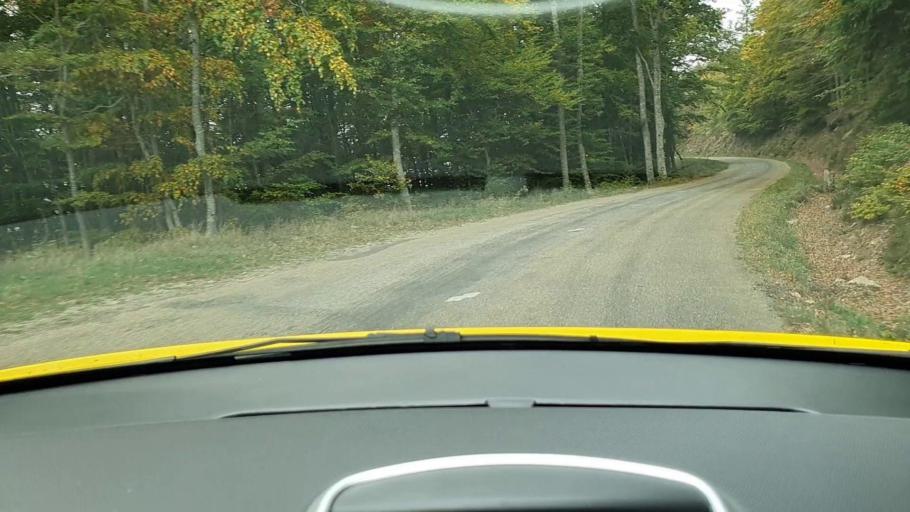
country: FR
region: Languedoc-Roussillon
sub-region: Departement de la Lozere
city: Meyrueis
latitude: 44.0871
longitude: 3.4261
